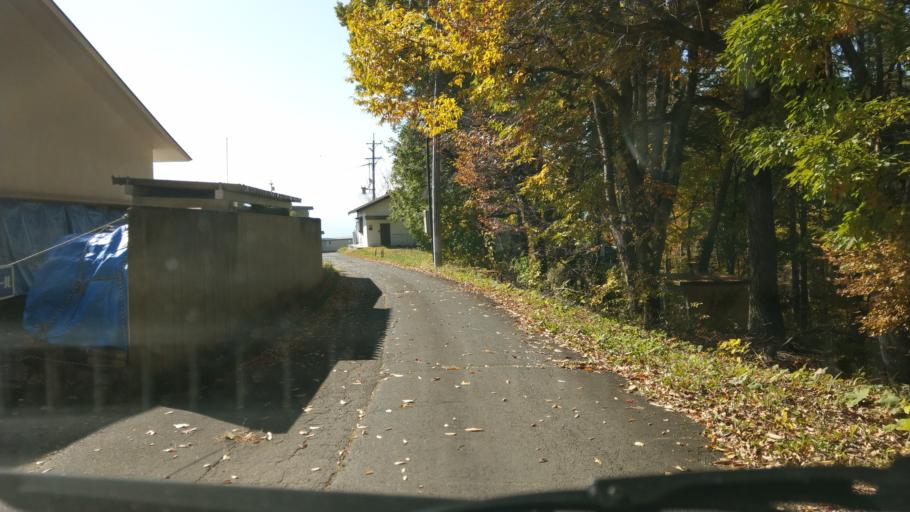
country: JP
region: Nagano
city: Komoro
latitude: 36.3610
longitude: 138.4475
